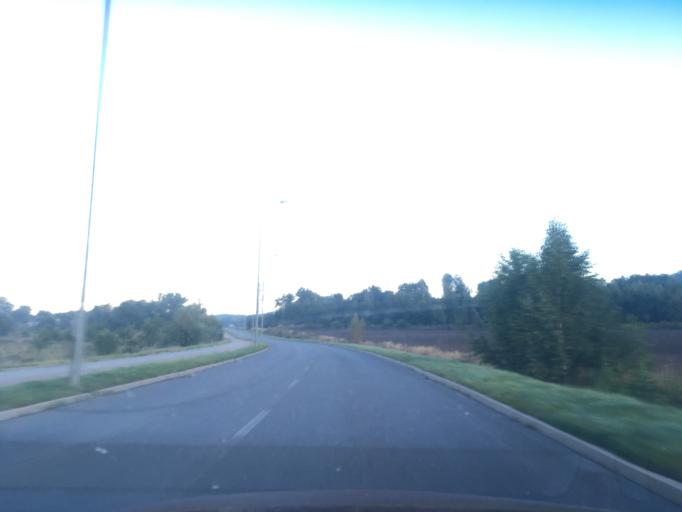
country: PL
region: Lower Silesian Voivodeship
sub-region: Powiat zgorzelecki
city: Bogatynia
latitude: 50.9126
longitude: 14.9639
